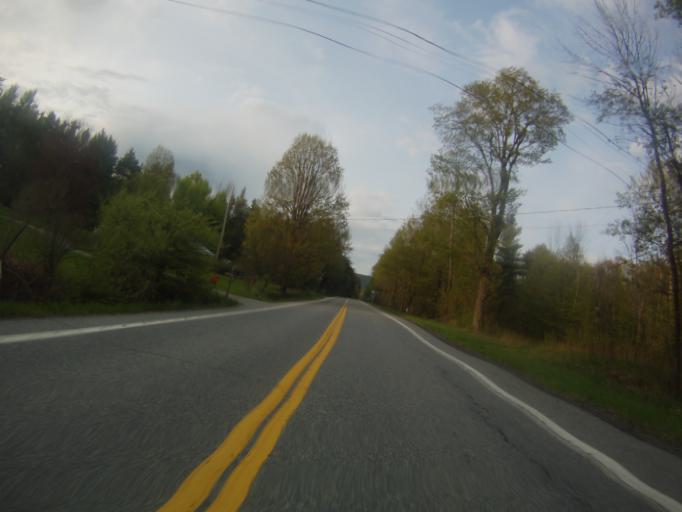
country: US
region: New York
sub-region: Essex County
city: Ticonderoga
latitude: 43.7508
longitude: -73.5633
